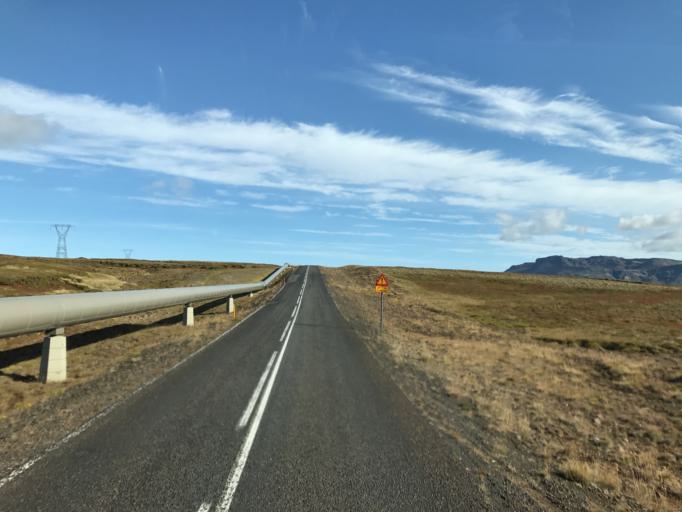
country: IS
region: Capital Region
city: Mosfellsbaer
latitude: 64.1177
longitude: -21.4649
